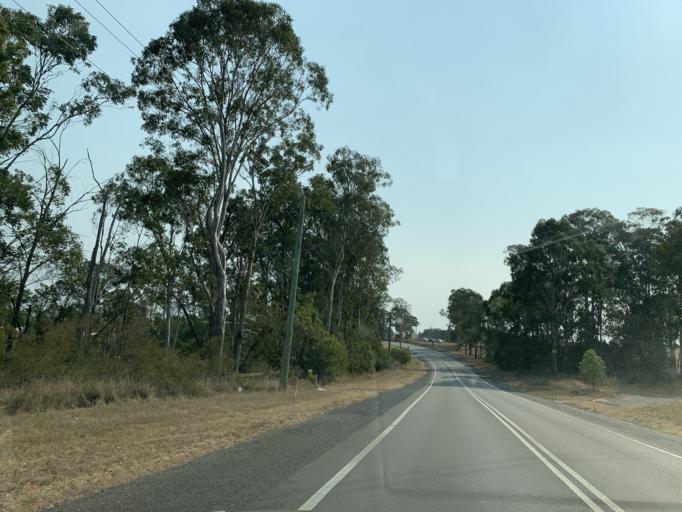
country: AU
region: New South Wales
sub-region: Blacktown
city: Rouse Hill
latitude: -33.6625
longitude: 150.9218
